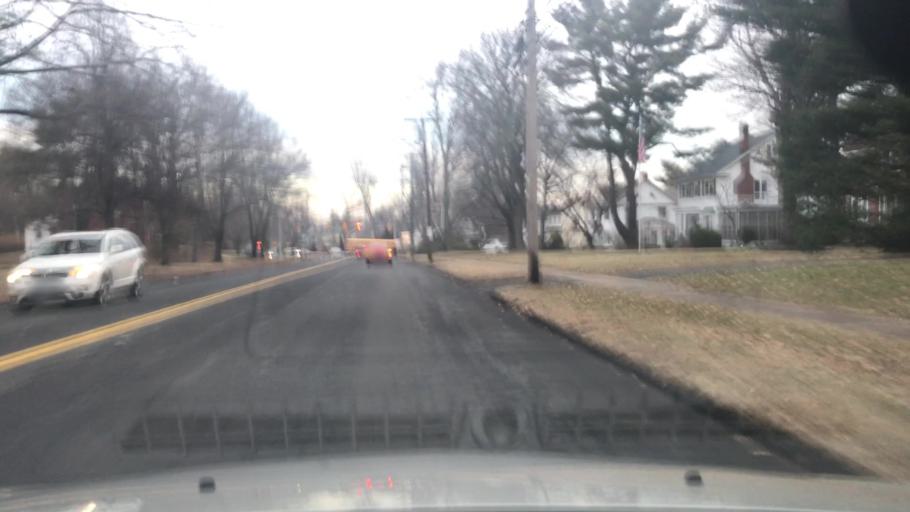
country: US
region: Connecticut
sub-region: Hartford County
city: Wethersfield
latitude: 41.7030
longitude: -72.6677
